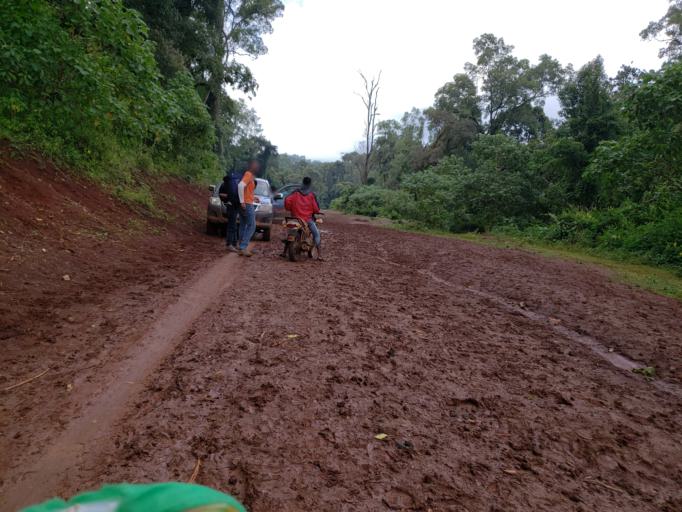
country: ET
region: Oromiya
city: Dodola
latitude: 6.4666
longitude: 39.5306
